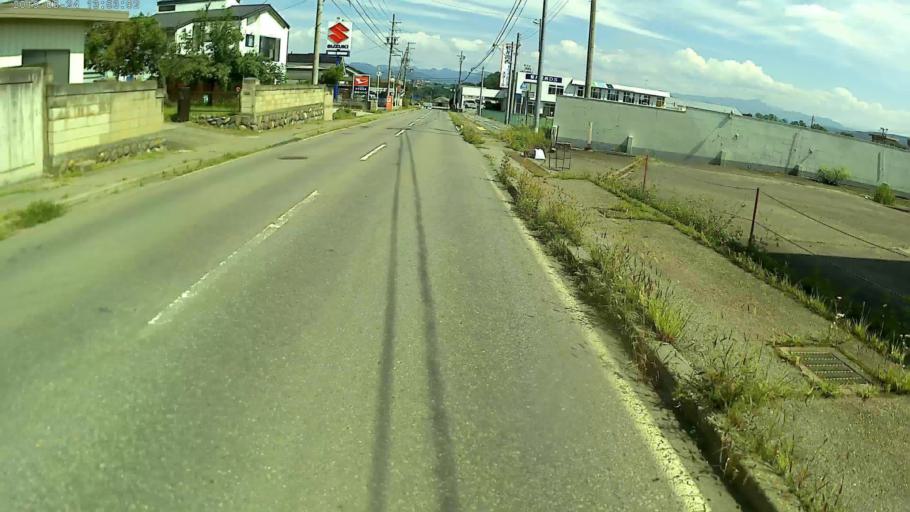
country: JP
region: Nagano
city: Komoro
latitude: 36.2735
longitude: 138.4095
